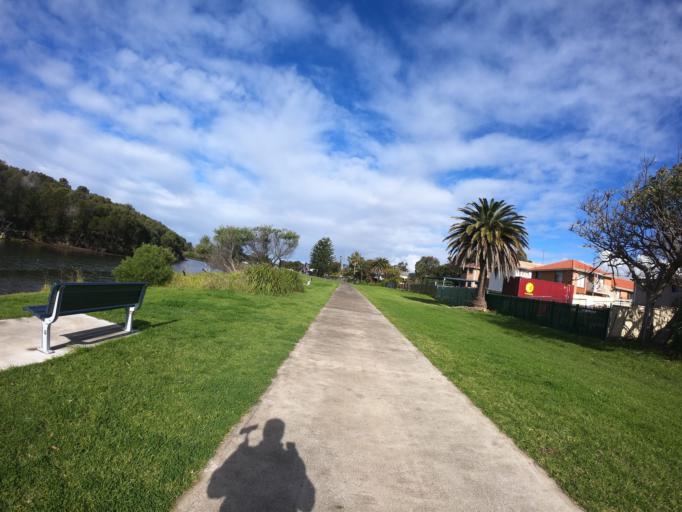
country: AU
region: New South Wales
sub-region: Wollongong
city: East Corrimal
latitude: -34.3748
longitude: 150.9193
